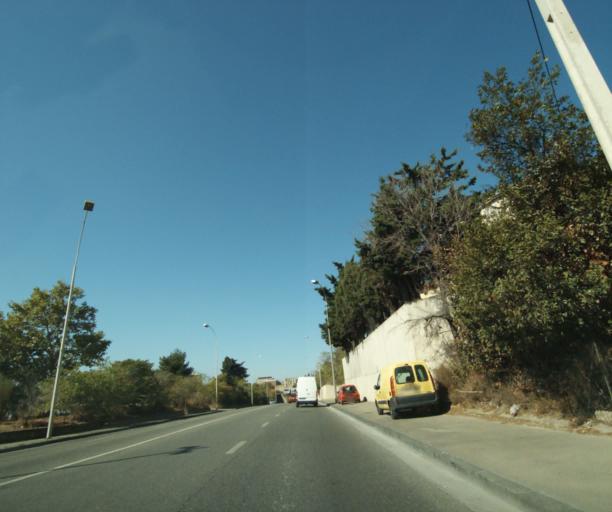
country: FR
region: Provence-Alpes-Cote d'Azur
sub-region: Departement des Bouches-du-Rhone
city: Marseille 14
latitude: 43.3395
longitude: 5.3911
